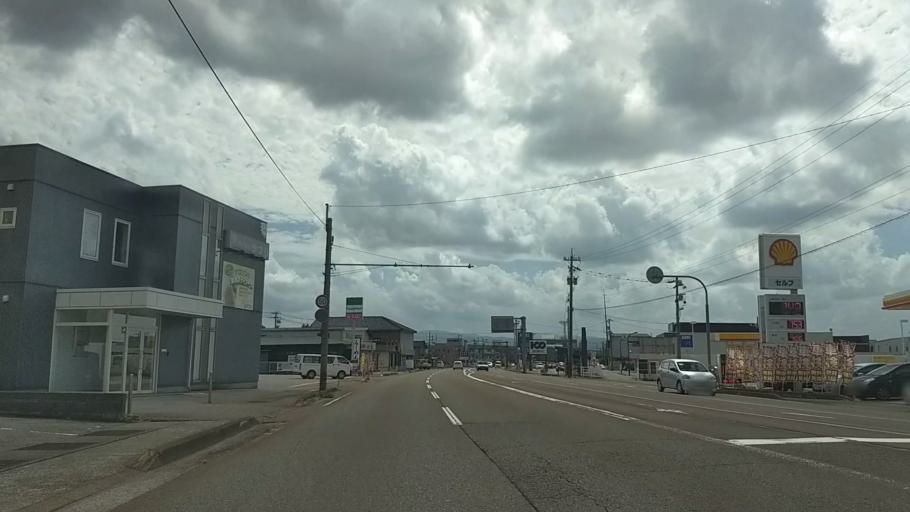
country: JP
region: Ishikawa
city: Kanazawa-shi
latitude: 36.5945
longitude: 136.6630
